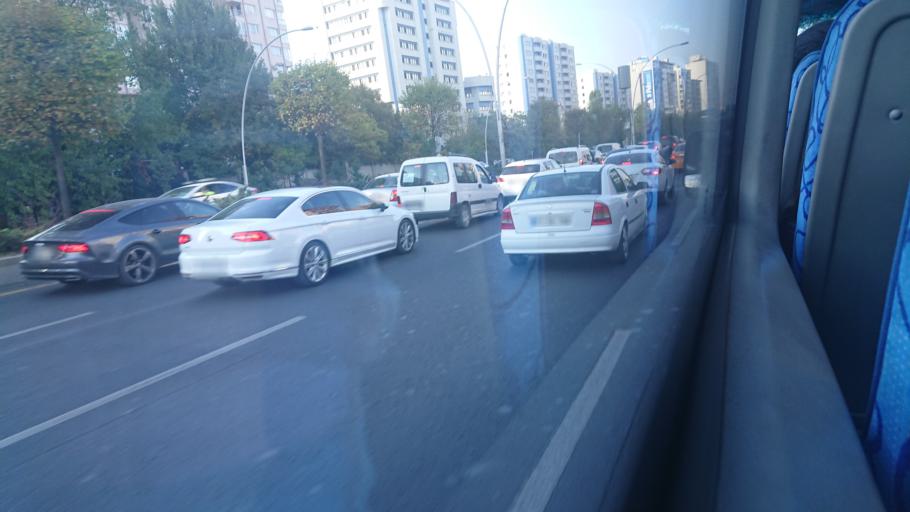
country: TR
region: Ankara
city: Ankara
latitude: 39.9257
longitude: 32.8158
